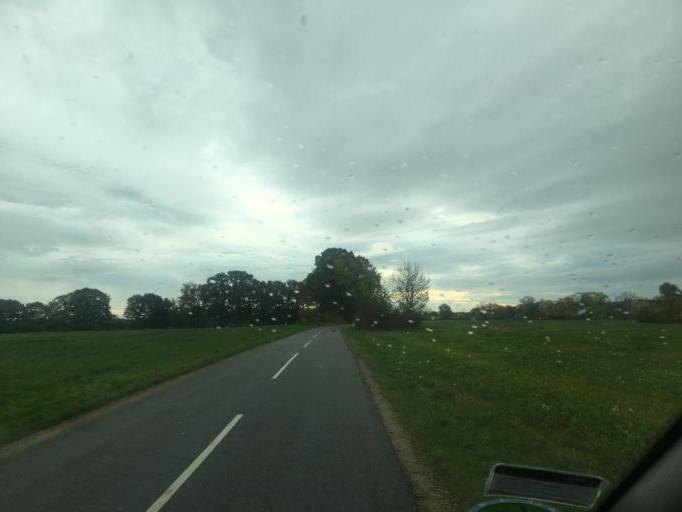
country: DK
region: Zealand
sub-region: Koge Kommune
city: Bjaeverskov
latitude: 55.4132
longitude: 11.9833
